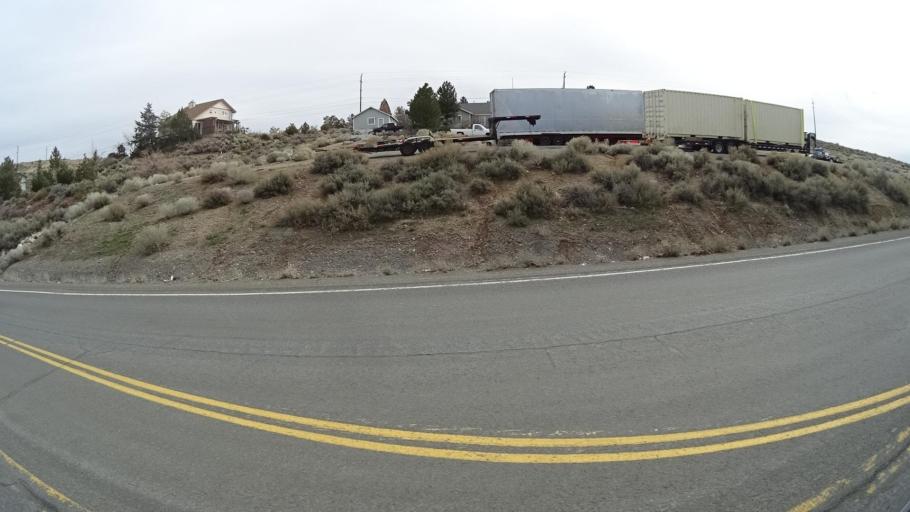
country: US
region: Nevada
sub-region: Washoe County
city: Golden Valley
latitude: 39.6041
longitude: -119.8090
